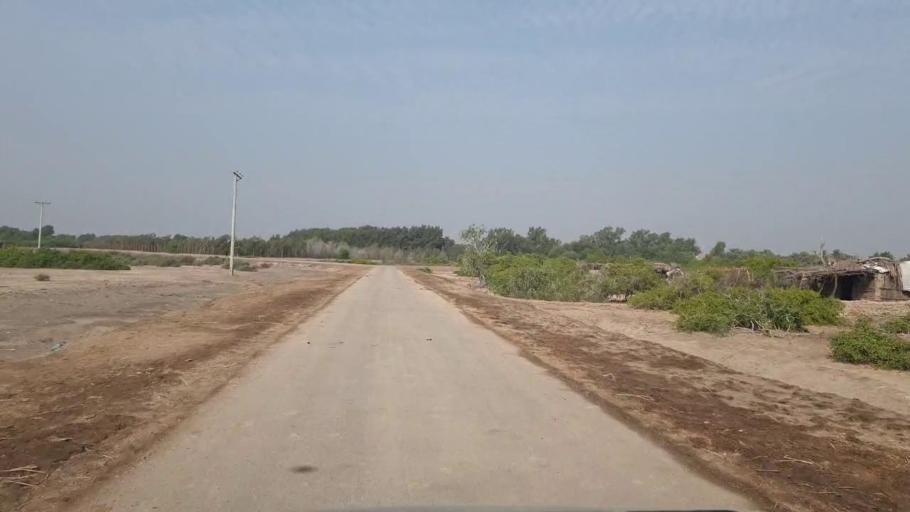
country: PK
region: Sindh
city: Tando Muhammad Khan
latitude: 25.1275
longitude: 68.4561
